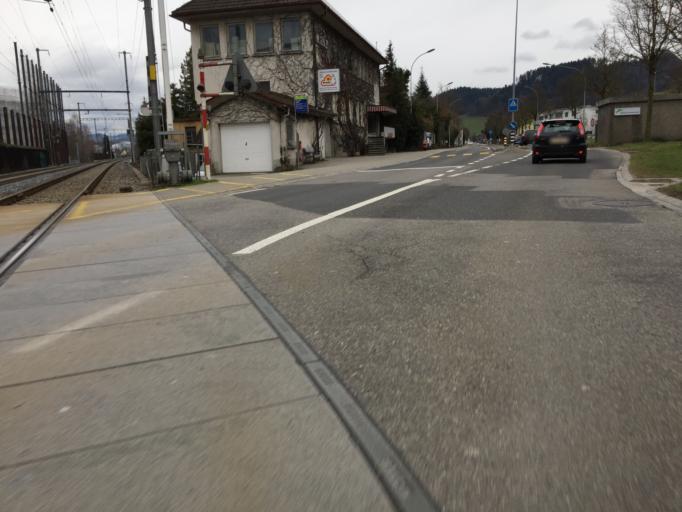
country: CH
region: Bern
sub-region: Emmental District
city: Oberburg
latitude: 47.0484
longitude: 7.6224
